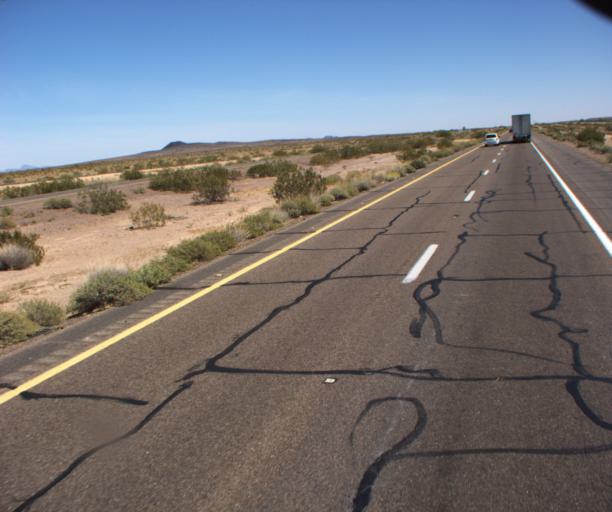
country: US
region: Arizona
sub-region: Maricopa County
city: Gila Bend
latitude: 32.8619
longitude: -113.1763
